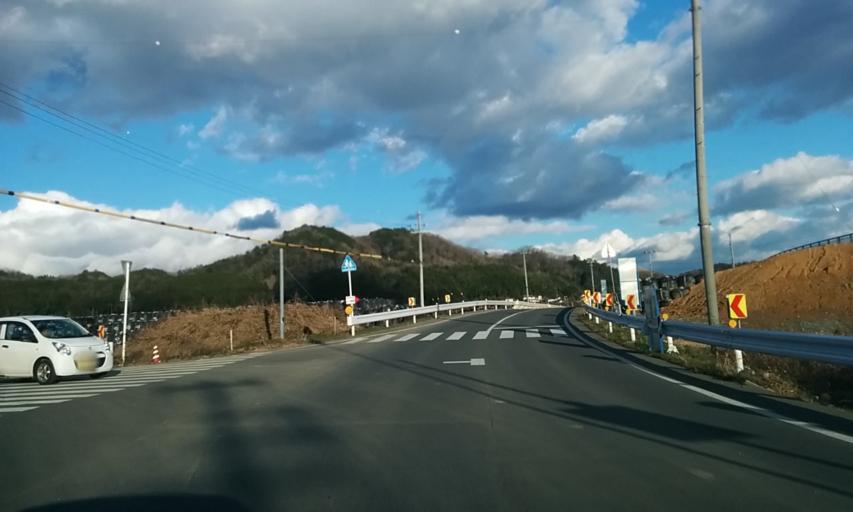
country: JP
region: Kyoto
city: Fukuchiyama
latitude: 35.3138
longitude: 135.1817
